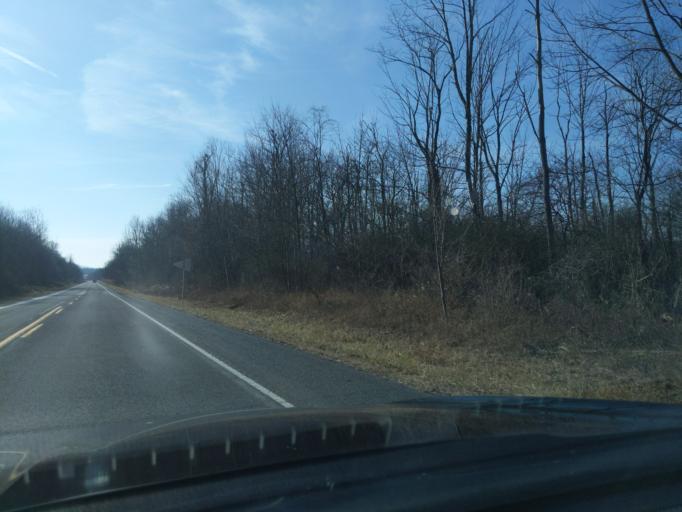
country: US
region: Pennsylvania
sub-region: Blair County
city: Bellwood
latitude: 40.6093
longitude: -78.3077
